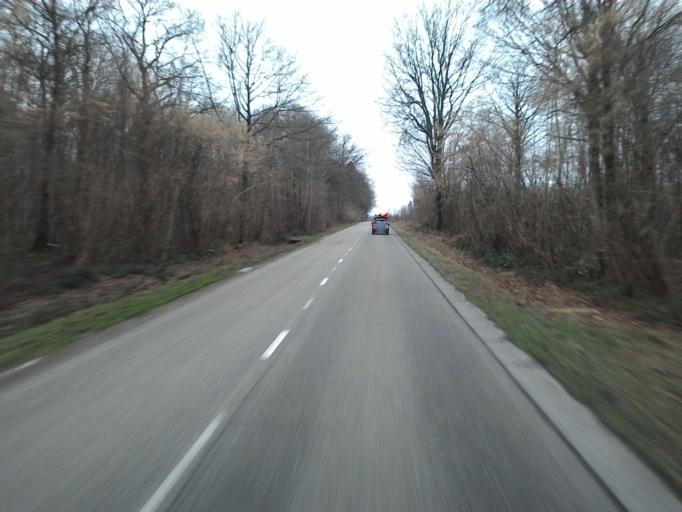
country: BE
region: Wallonia
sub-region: Province de Namur
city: Beauraing
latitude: 50.0459
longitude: 4.9687
